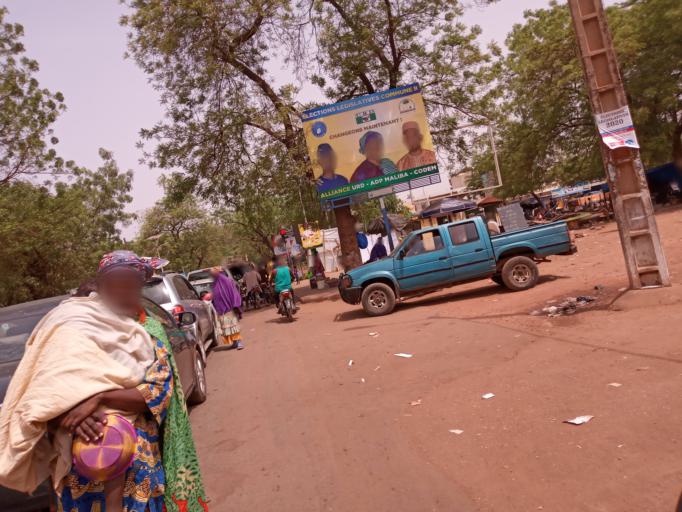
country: ML
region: Bamako
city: Bamako
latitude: 12.6527
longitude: -7.9816
